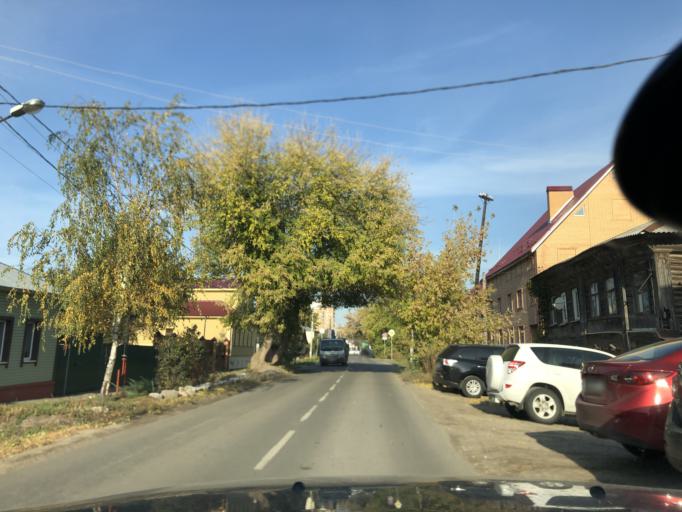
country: RU
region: Tula
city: Tula
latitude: 54.1903
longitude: 37.6306
